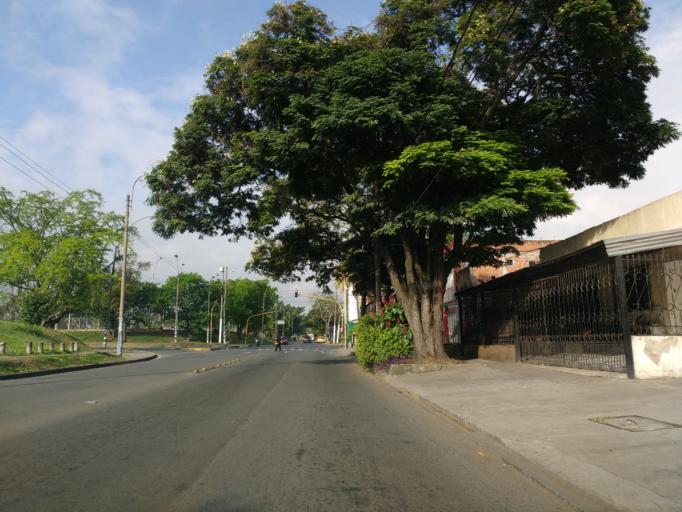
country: CO
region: Valle del Cauca
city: Cali
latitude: 3.4756
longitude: -76.5140
